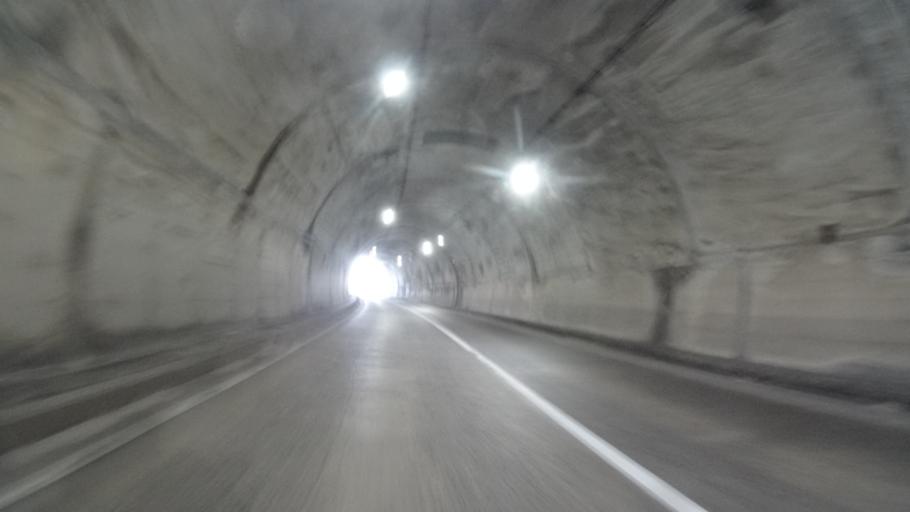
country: JP
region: Ishikawa
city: Nanao
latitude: 37.1327
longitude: 136.7275
